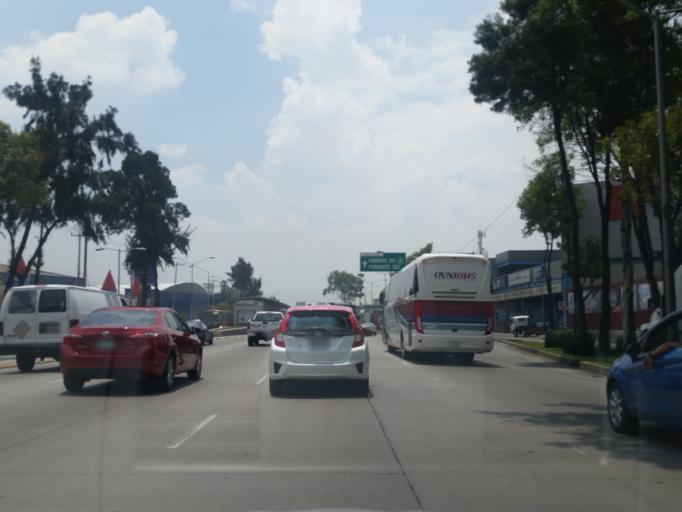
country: MX
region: Mexico
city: Colonia Lindavista
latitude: 19.4940
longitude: -99.1538
